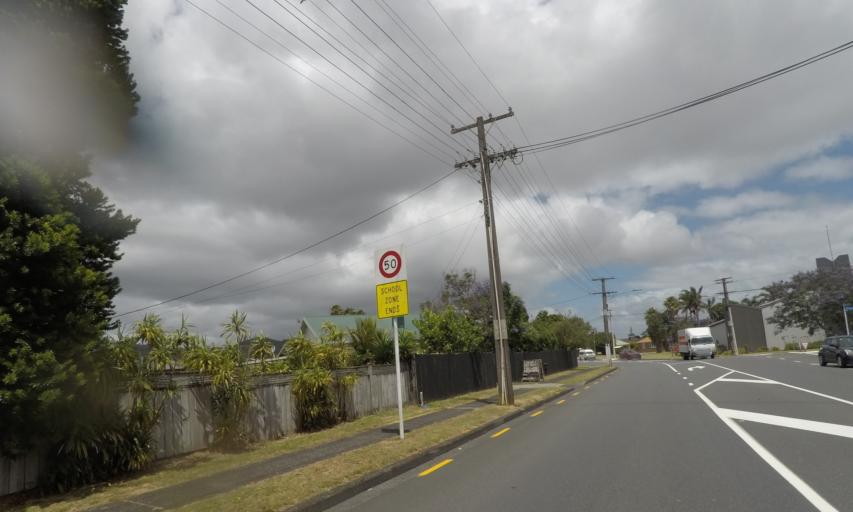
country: NZ
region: Northland
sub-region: Whangarei
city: Whangarei
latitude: -35.7022
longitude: 174.3153
